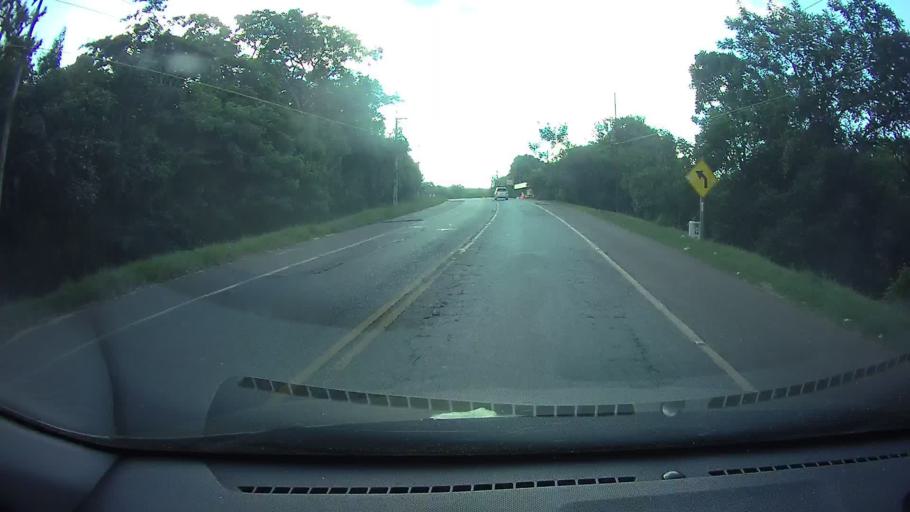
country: PY
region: Cordillera
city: Eusebio Ayala
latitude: -25.3768
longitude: -57.0254
